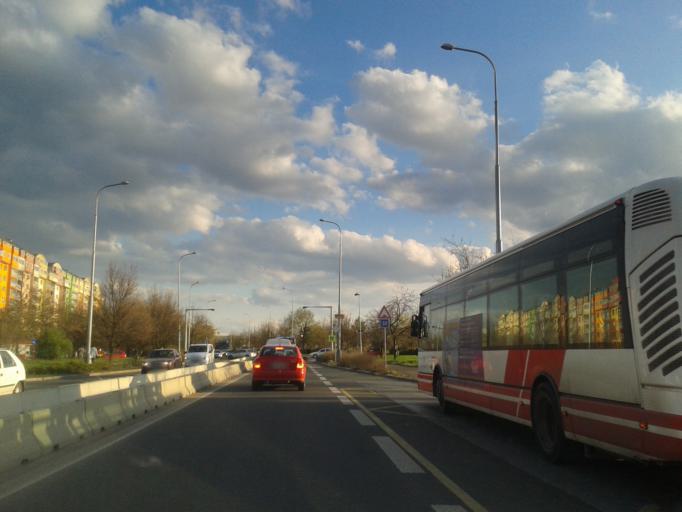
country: CZ
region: Praha
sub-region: Praha 18
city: Letnany
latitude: 50.1393
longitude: 14.5047
